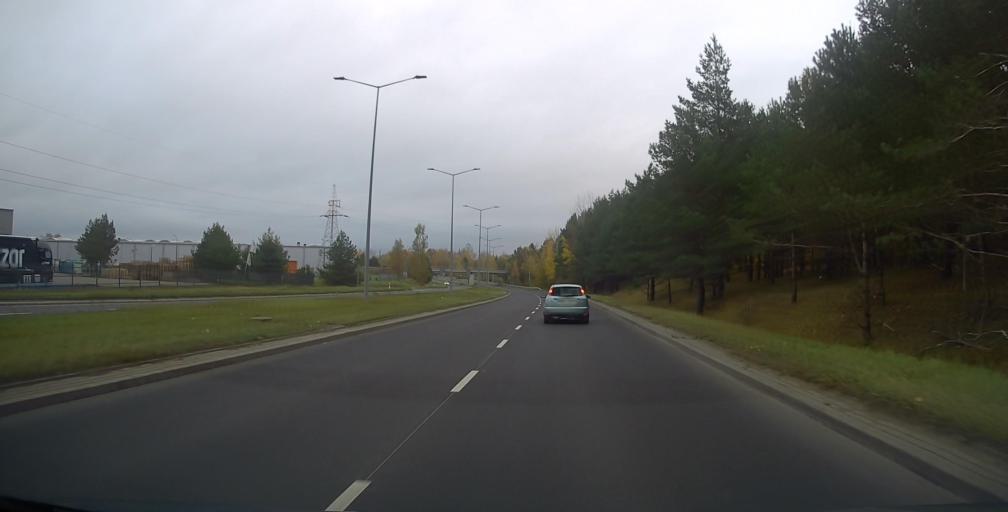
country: PL
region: Warmian-Masurian Voivodeship
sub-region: Powiat elcki
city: Elk
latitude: 53.8158
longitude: 22.3855
